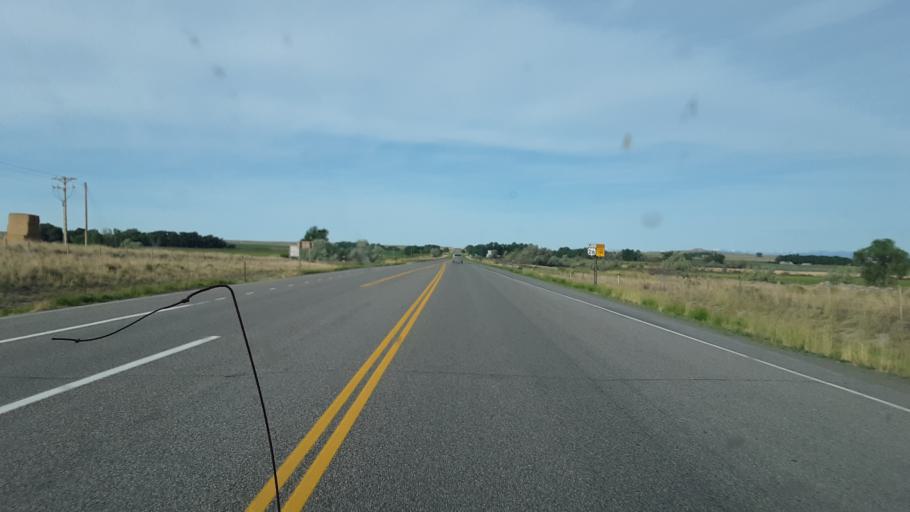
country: US
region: Wyoming
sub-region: Fremont County
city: Riverton
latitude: 43.1854
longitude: -108.2460
